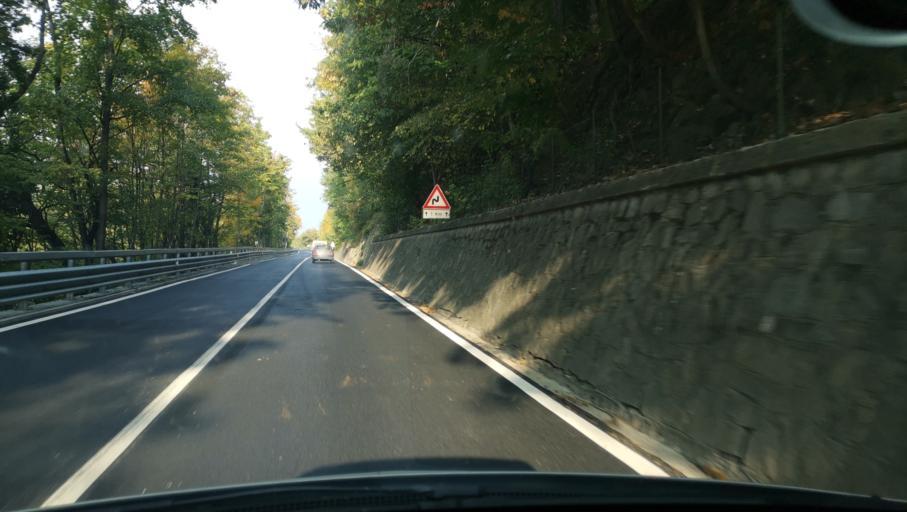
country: IT
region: Piedmont
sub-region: Provincia di Torino
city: Chiomonte
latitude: 45.1102
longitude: 6.9636
